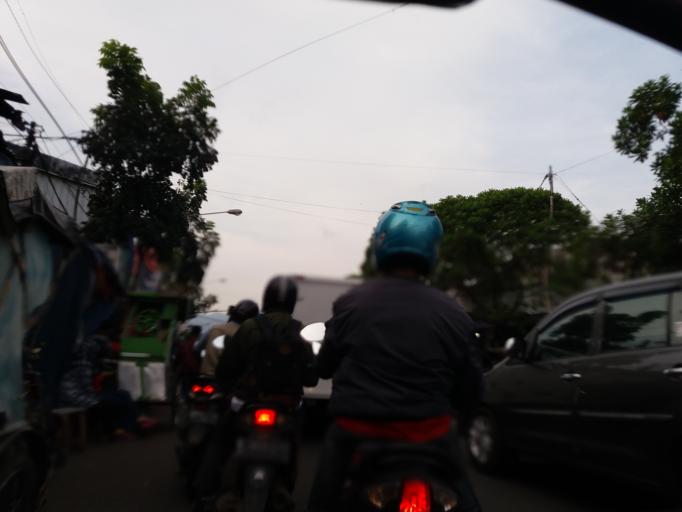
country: ID
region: West Java
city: Bandung
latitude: -6.9091
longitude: 107.6424
